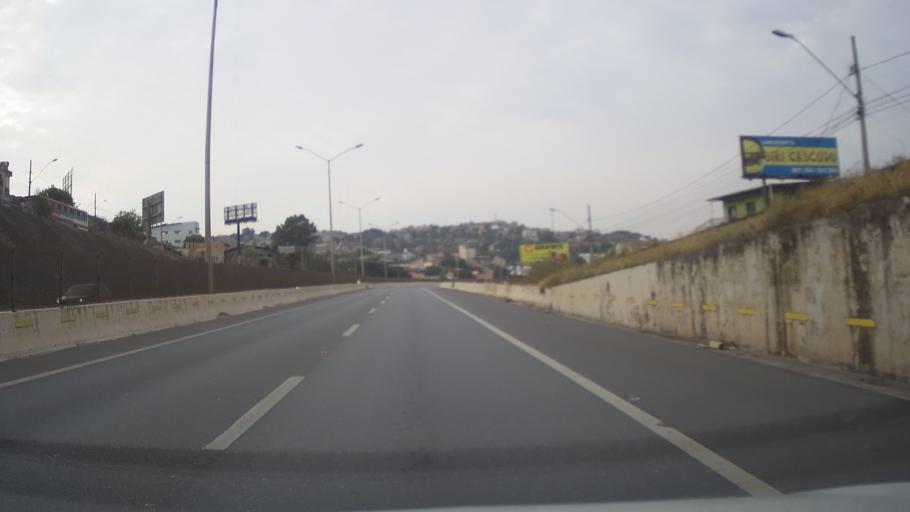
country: BR
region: Minas Gerais
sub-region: Vespasiano
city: Vespasiano
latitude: -19.7521
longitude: -43.9487
